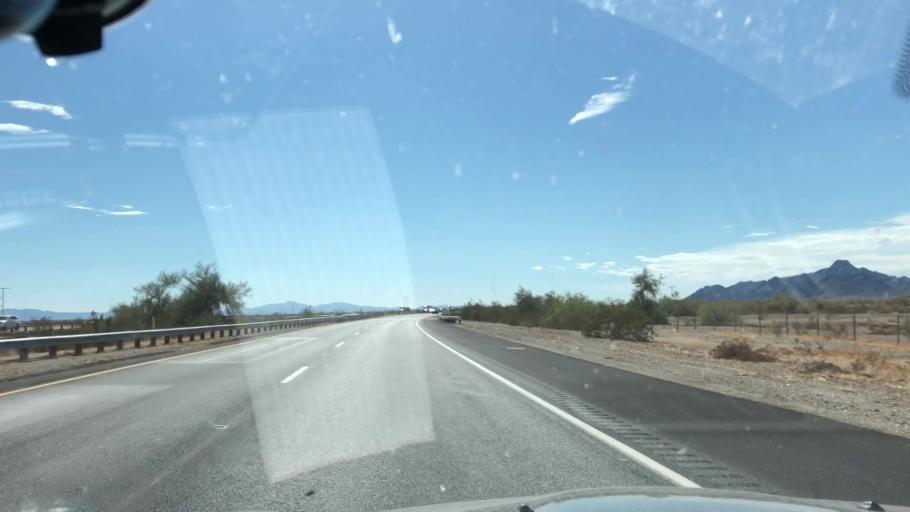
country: US
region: California
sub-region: Riverside County
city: Mesa Verde
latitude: 33.6091
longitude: -114.7689
